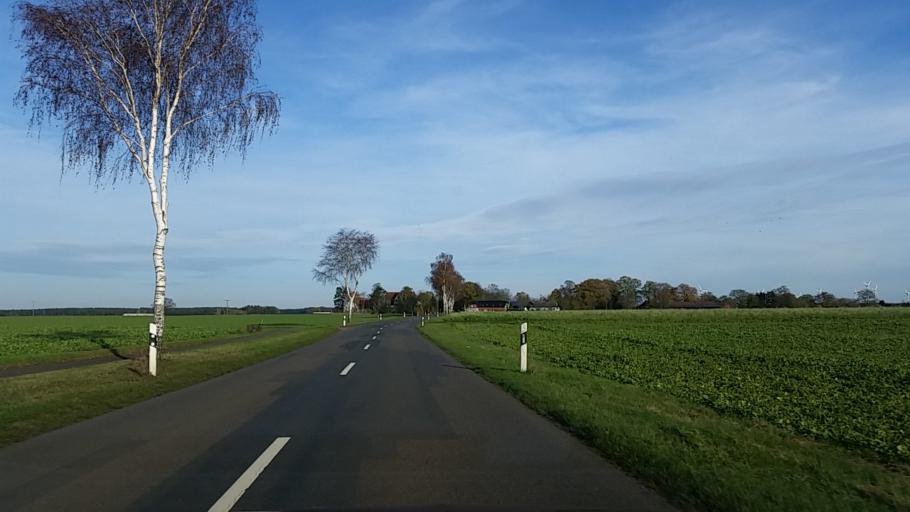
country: DE
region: Lower Saxony
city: Gross Oesingen
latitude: 52.6541
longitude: 10.4773
